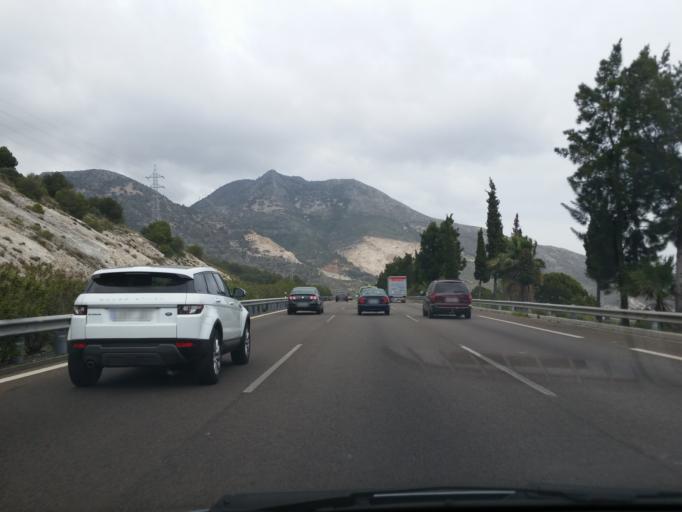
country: ES
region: Andalusia
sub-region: Provincia de Malaga
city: Benalmadena
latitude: 36.5960
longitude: -4.5765
